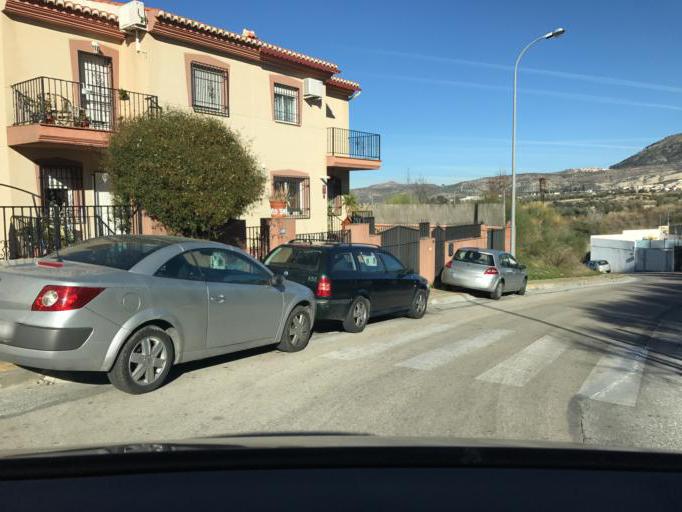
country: ES
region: Andalusia
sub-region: Provincia de Granada
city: Alfacar
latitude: 37.2194
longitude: -3.5721
